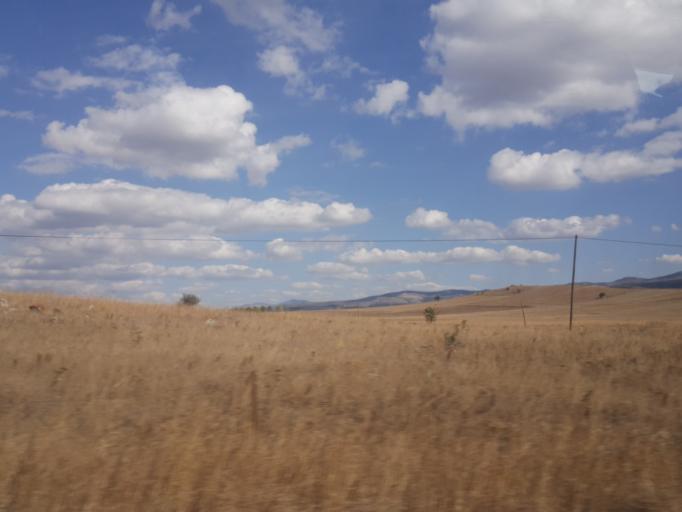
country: TR
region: Tokat
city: Artova
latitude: 40.0472
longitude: 36.3006
